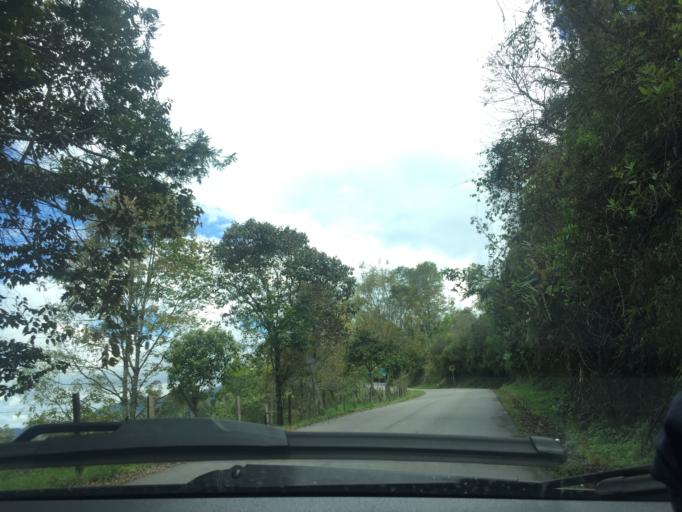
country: CO
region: Cundinamarca
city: Supata
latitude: 5.0537
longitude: -74.2467
